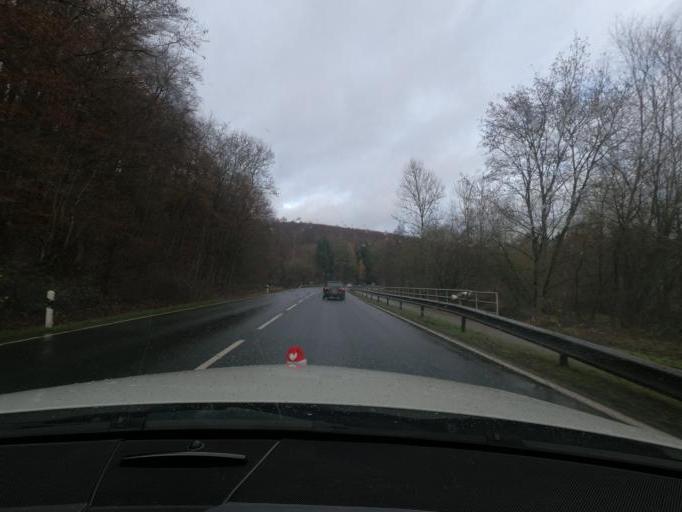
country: DE
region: Lower Saxony
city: Kreiensen
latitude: 51.8651
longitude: 9.9621
